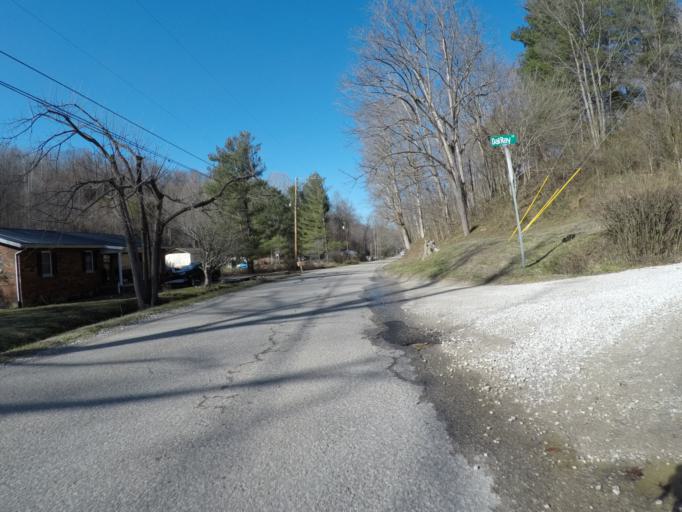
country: US
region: Kentucky
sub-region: Boyd County
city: Catlettsburg
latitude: 38.4069
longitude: -82.6374
